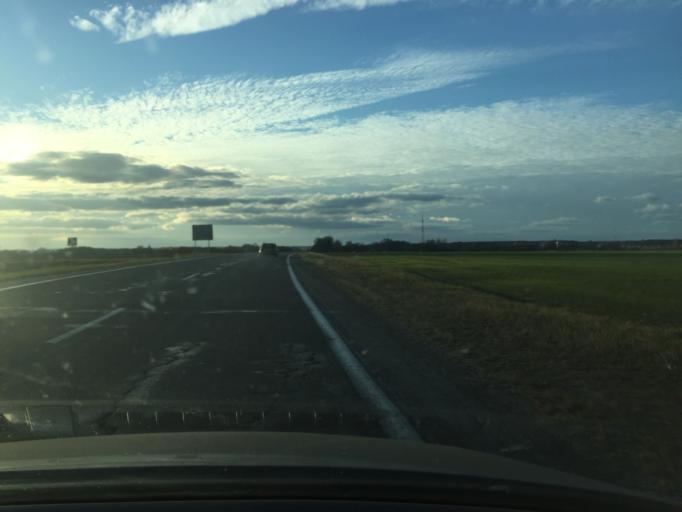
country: BY
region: Vitebsk
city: Vyerkhnyadzvinsk
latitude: 55.8366
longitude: 27.9040
